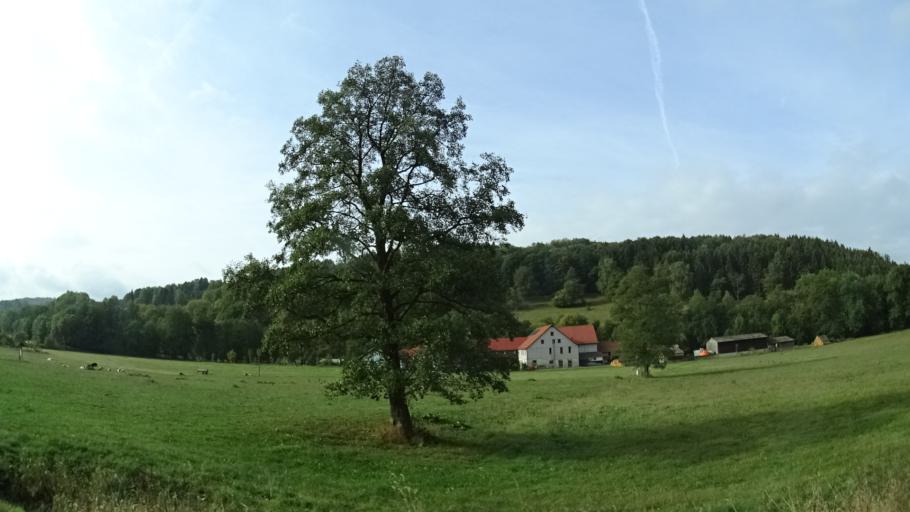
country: DE
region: Hesse
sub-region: Regierungsbezirk Kassel
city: Hilders
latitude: 50.5787
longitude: 9.9949
